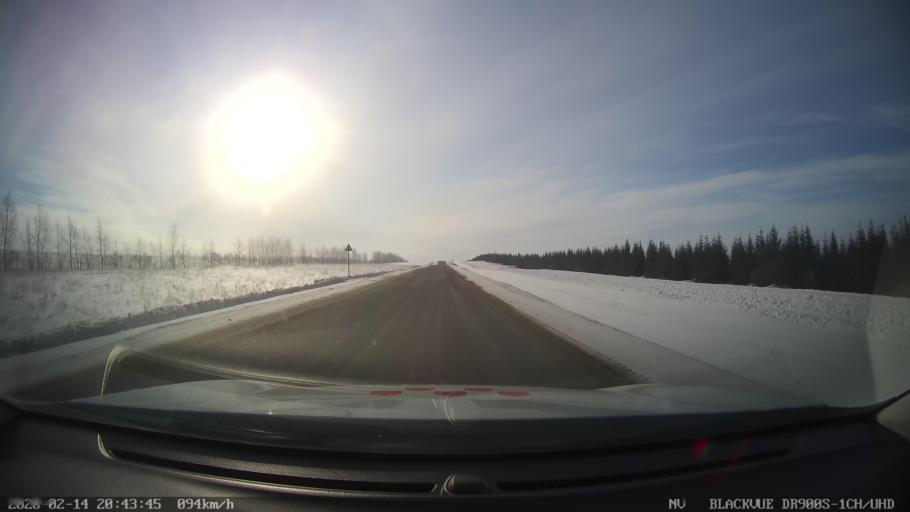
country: RU
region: Tatarstan
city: Kuybyshevskiy Zaton
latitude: 55.3039
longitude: 49.1481
